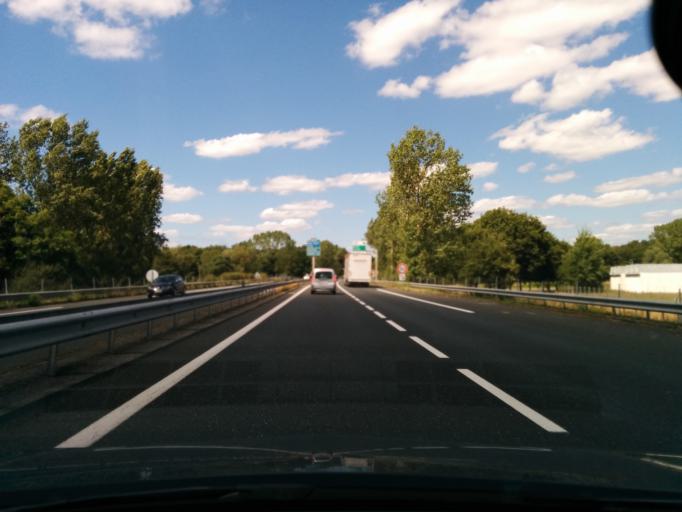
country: FR
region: Centre
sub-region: Departement du Cher
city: Vierzon
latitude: 47.2273
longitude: 2.0378
